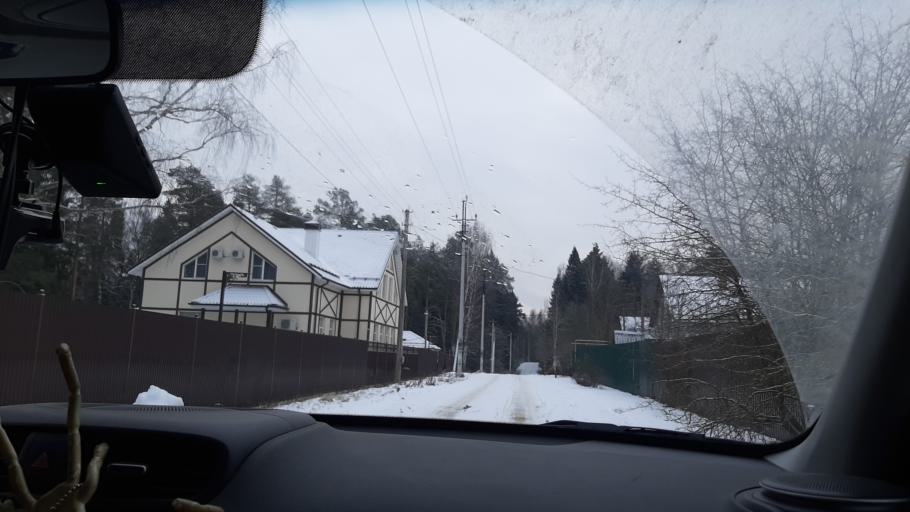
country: RU
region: Ivanovo
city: Kokhma
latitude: 56.9002
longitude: 41.0088
